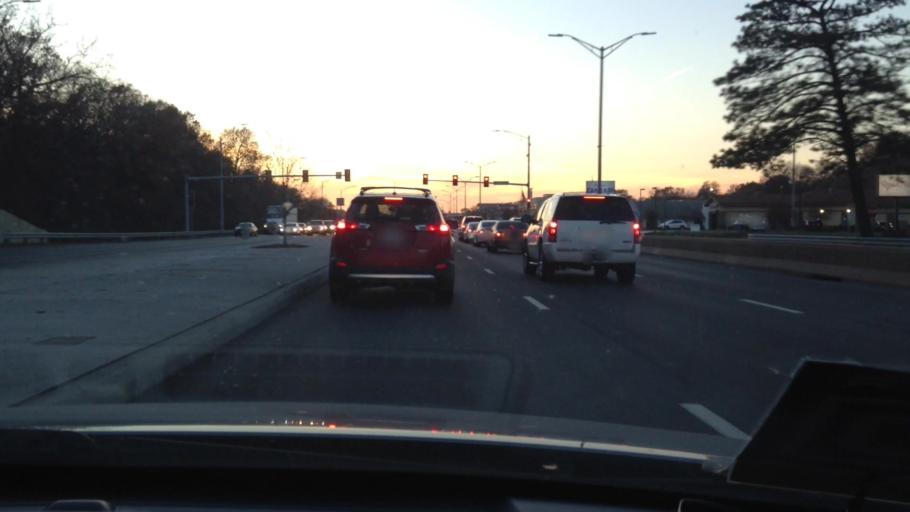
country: US
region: Kansas
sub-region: Johnson County
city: Merriam
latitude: 39.0150
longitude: -94.7028
